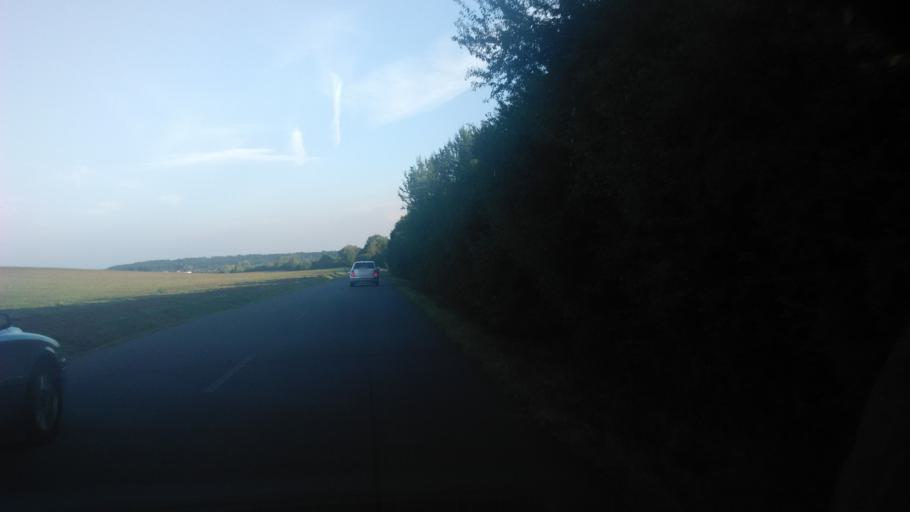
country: SK
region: Banskobystricky
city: Dudince
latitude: 48.1933
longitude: 18.8273
